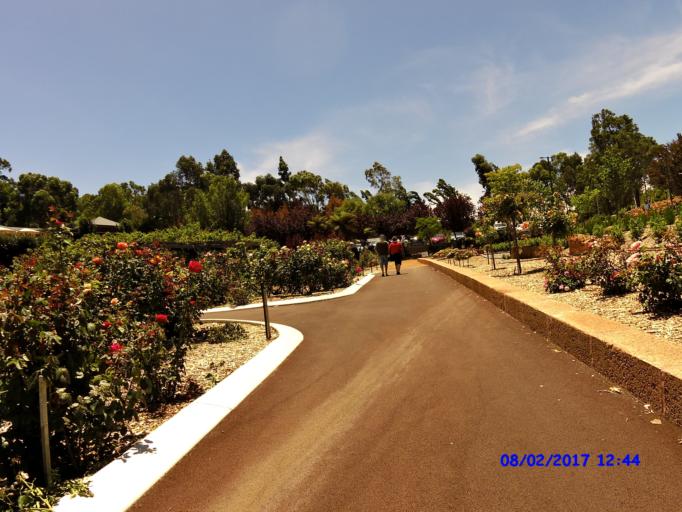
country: AU
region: Western Australia
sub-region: Kalamunda
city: Gooseberry Hill
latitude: -32.0258
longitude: 116.0733
